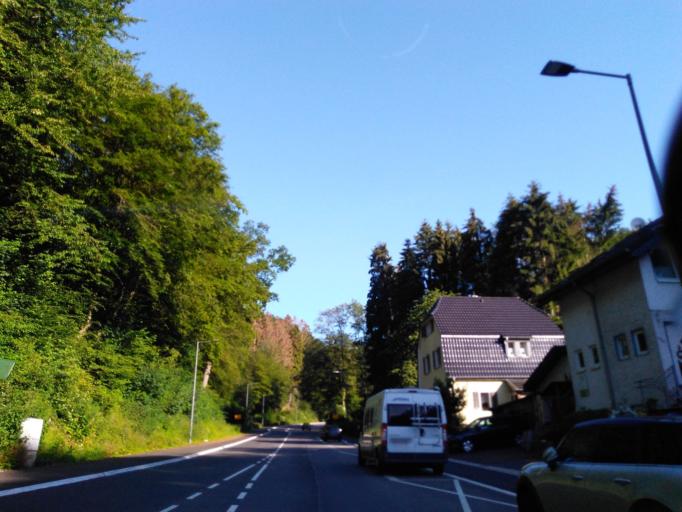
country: DE
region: North Rhine-Westphalia
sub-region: Regierungsbezirk Koln
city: Overath
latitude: 50.9335
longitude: 7.2804
